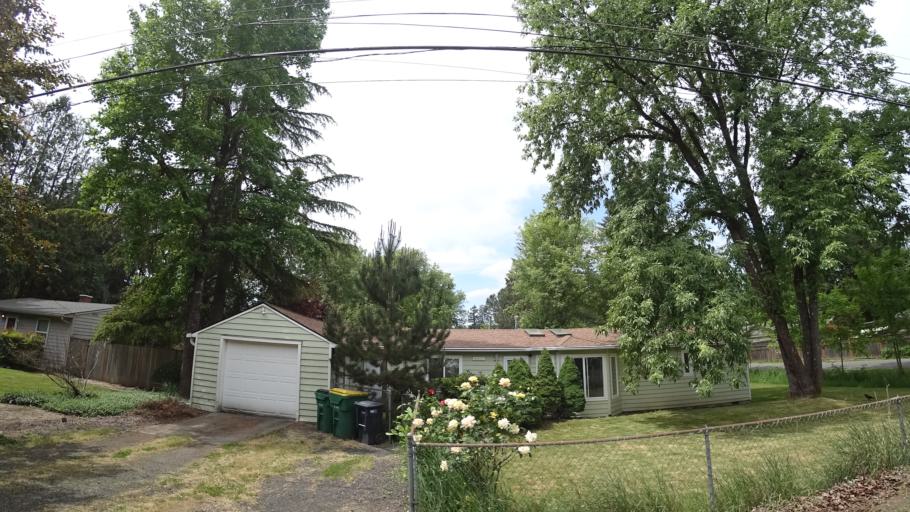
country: US
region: Oregon
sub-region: Washington County
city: Metzger
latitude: 45.4476
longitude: -122.7615
